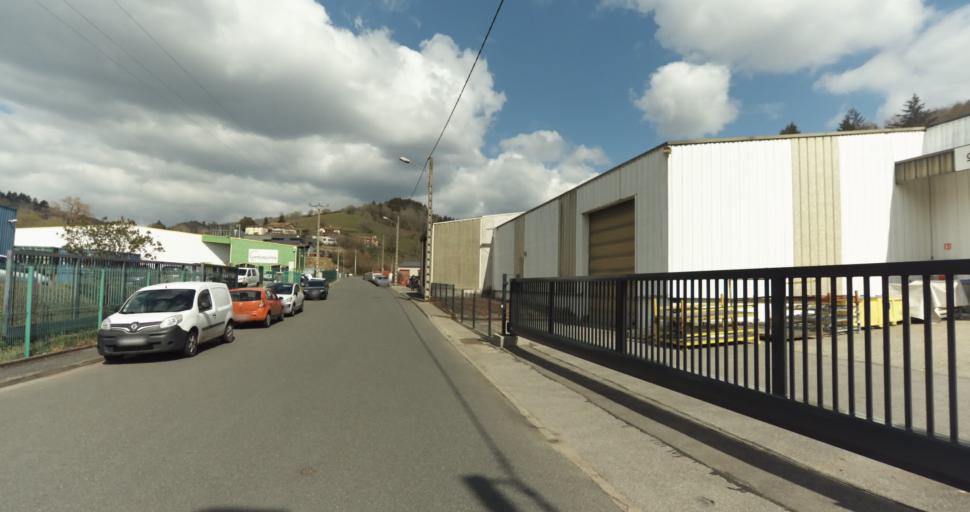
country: FR
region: Rhone-Alpes
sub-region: Departement du Rhone
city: Tarare
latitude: 45.9110
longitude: 4.4263
